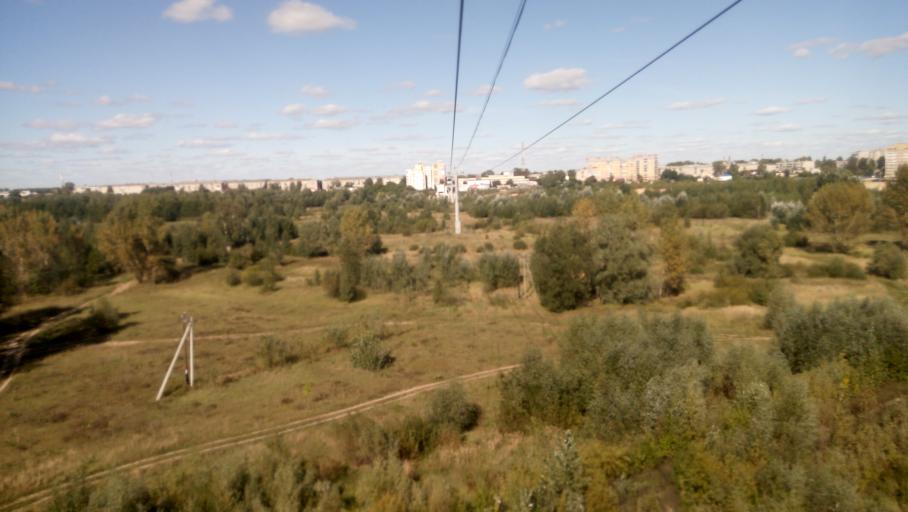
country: RU
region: Nizjnij Novgorod
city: Bor
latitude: 56.3474
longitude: 44.0564
